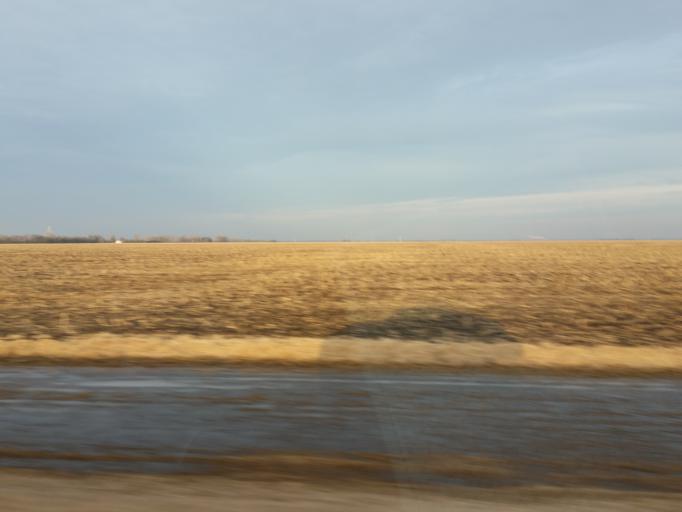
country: US
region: North Dakota
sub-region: Traill County
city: Mayville
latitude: 47.4612
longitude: -97.3260
